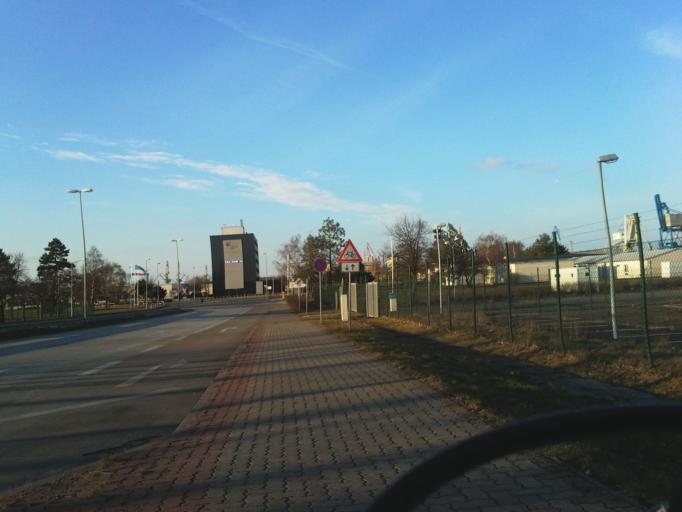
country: DE
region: Mecklenburg-Vorpommern
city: Warnemuende
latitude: 54.1428
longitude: 12.1097
